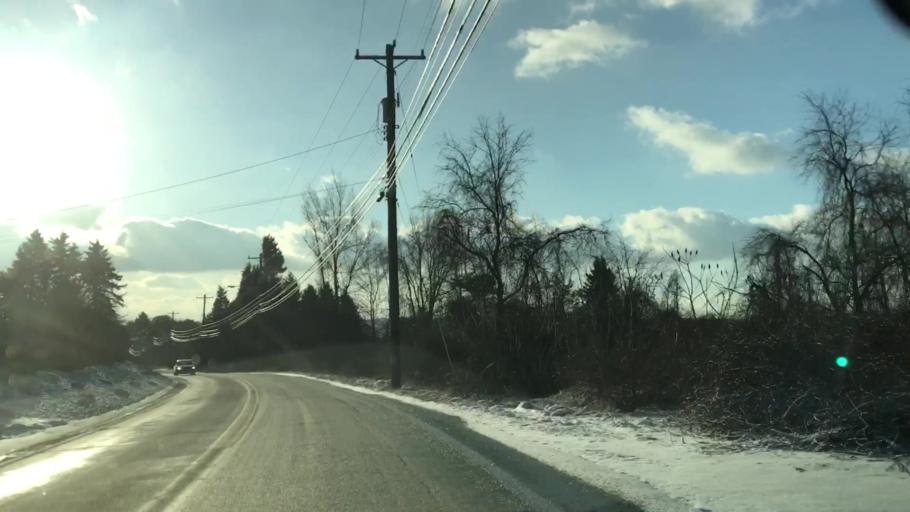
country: US
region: Pennsylvania
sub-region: Allegheny County
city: Enlow
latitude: 40.4737
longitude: -80.1894
